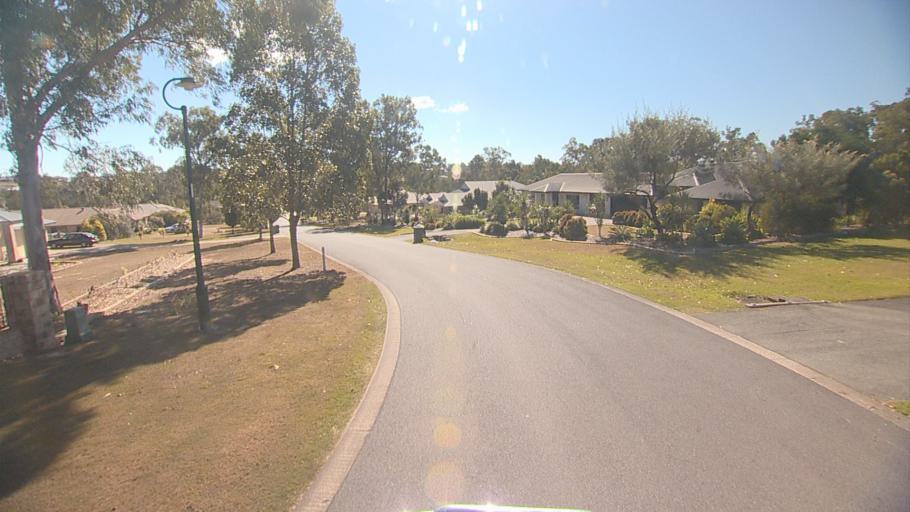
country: AU
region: Queensland
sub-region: Logan
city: North Maclean
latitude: -27.7584
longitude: 152.9522
